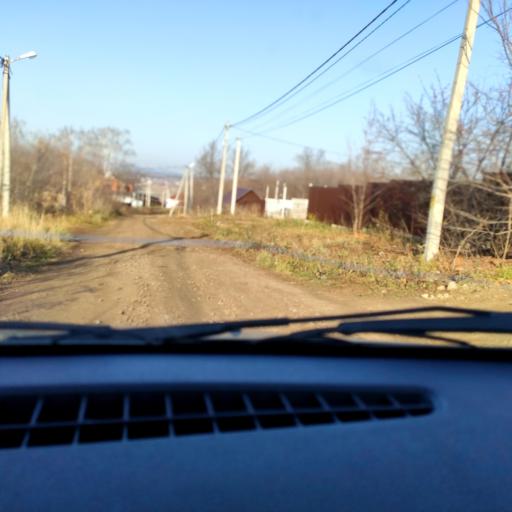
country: RU
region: Bashkortostan
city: Kabakovo
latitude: 54.6294
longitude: 56.0702
